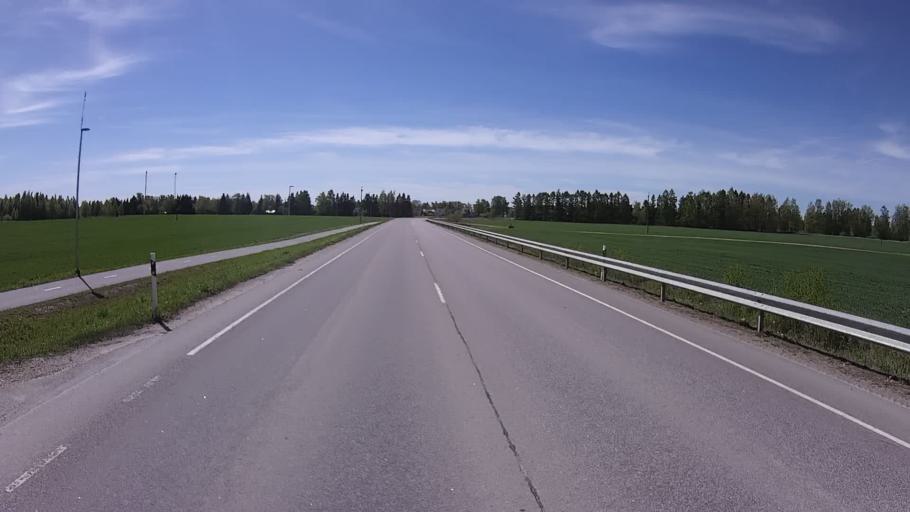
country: EE
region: Polvamaa
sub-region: Polva linn
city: Polva
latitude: 58.0752
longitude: 27.0884
